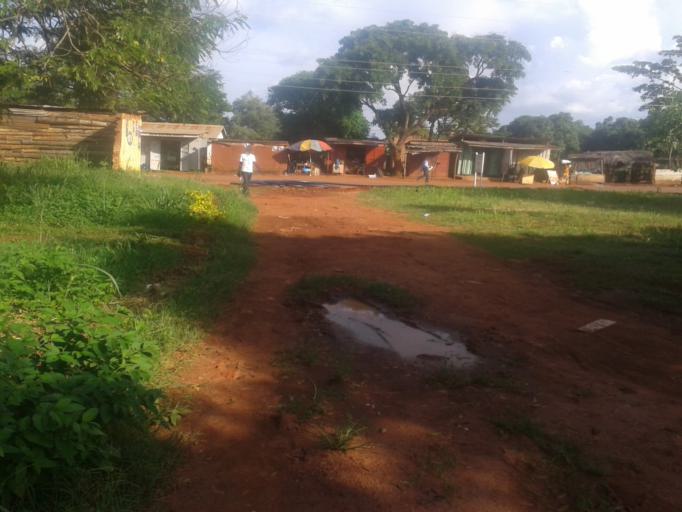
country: UG
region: Northern Region
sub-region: Gulu District
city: Gulu
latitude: 2.7875
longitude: 32.3156
